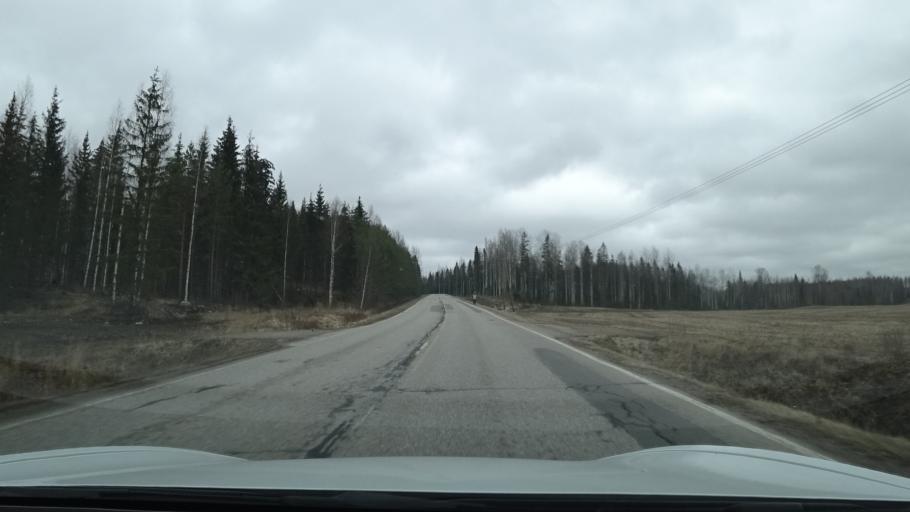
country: FI
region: Uusimaa
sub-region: Porvoo
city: Pukkila
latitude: 60.6442
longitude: 25.6466
